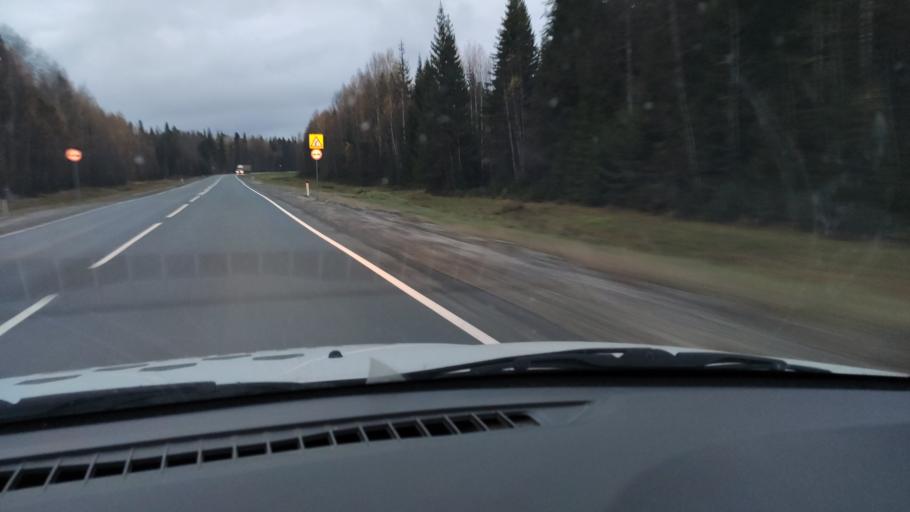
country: RU
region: Kirov
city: Kostino
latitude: 58.8560
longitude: 53.1006
